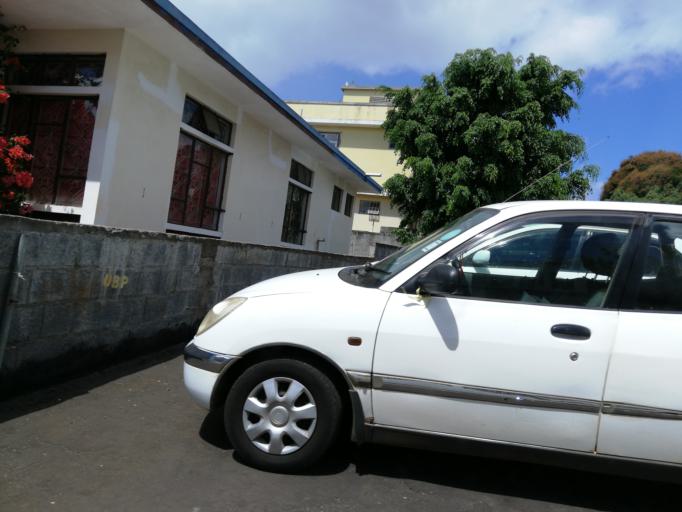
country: MU
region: Moka
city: Pailles
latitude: -20.2023
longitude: 57.4715
